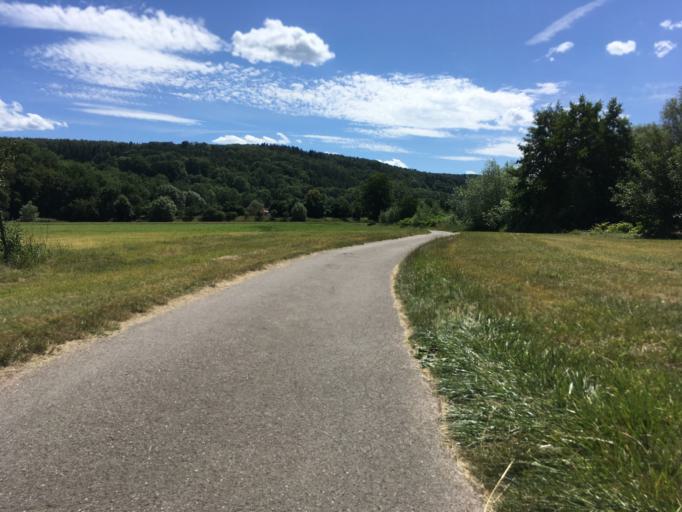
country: DE
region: Baden-Wuerttemberg
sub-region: Karlsruhe Region
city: Muhlacker
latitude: 48.9336
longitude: 8.8722
